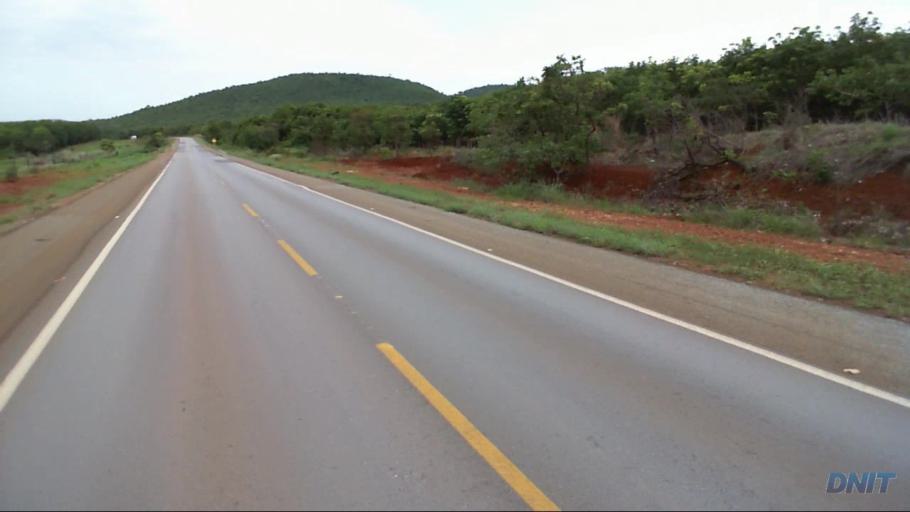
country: BR
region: Goias
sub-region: Barro Alto
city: Barro Alto
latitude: -14.9021
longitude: -48.9635
